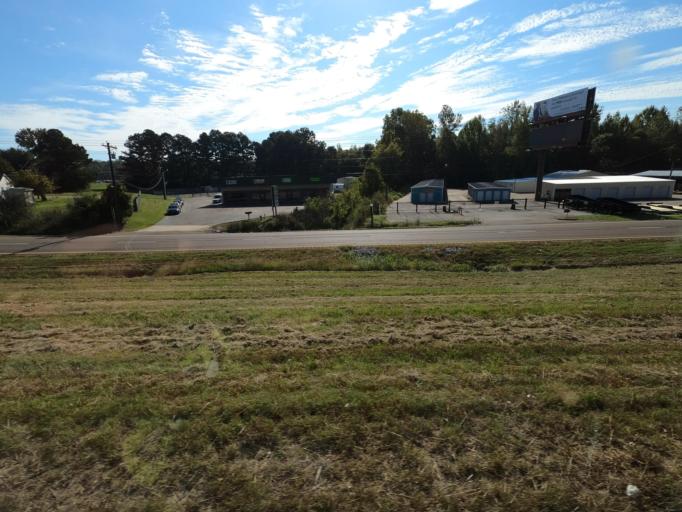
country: US
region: Tennessee
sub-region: Tipton County
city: Munford
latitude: 35.4197
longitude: -89.8211
